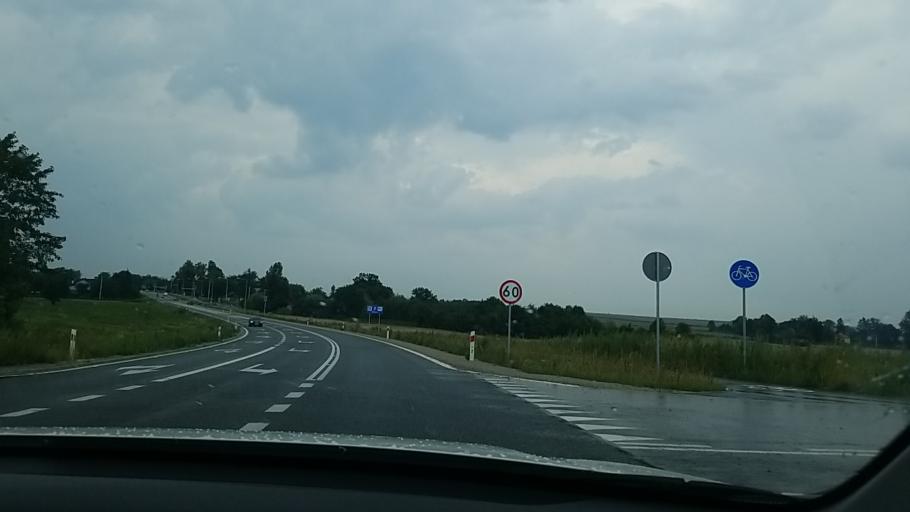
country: PL
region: Lublin Voivodeship
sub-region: Powiat lubelski
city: Krzczonow
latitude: 50.9765
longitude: 22.6812
